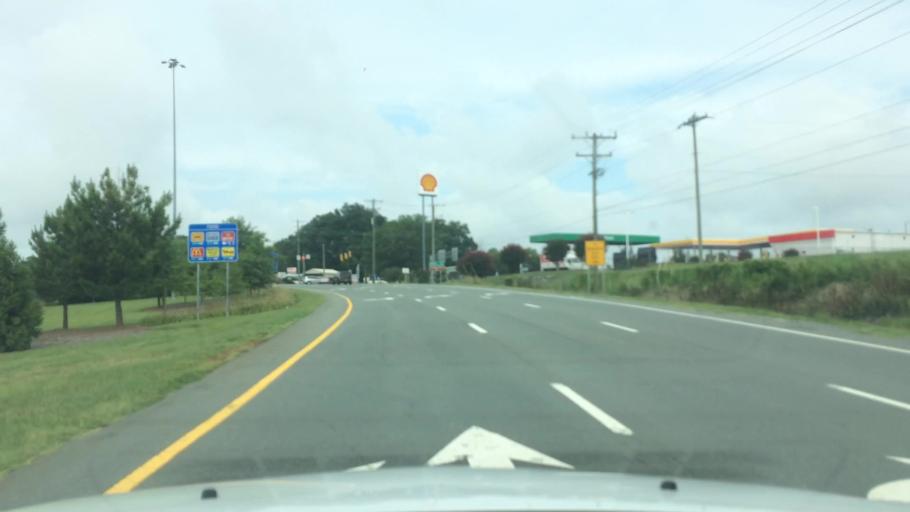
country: US
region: North Carolina
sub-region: Alamance County
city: Mebane
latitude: 36.0723
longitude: -79.2703
